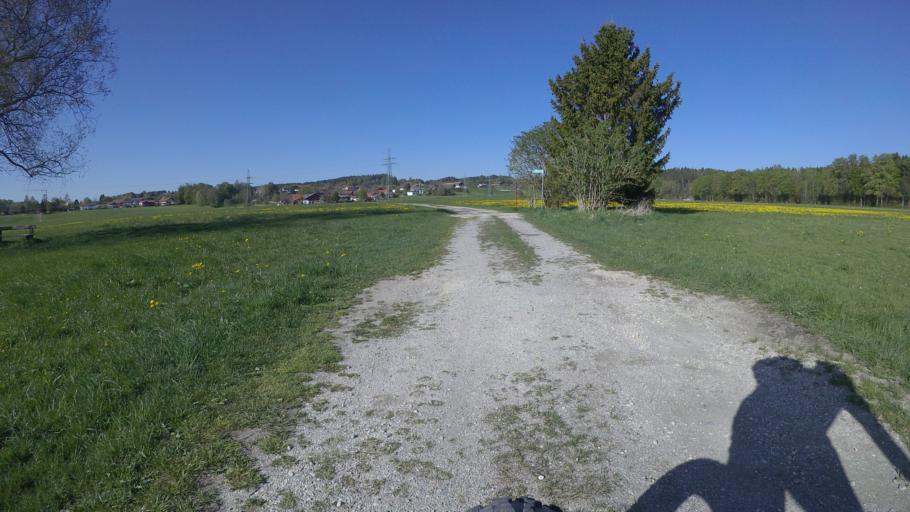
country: DE
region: Bavaria
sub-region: Upper Bavaria
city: Grabenstatt
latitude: 47.8464
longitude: 12.5589
